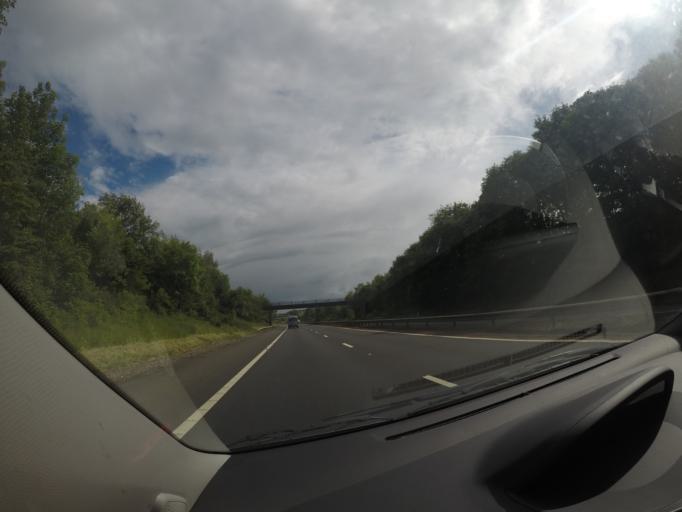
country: GB
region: Scotland
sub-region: Stirling
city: Stirling
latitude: 56.0936
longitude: -3.9488
